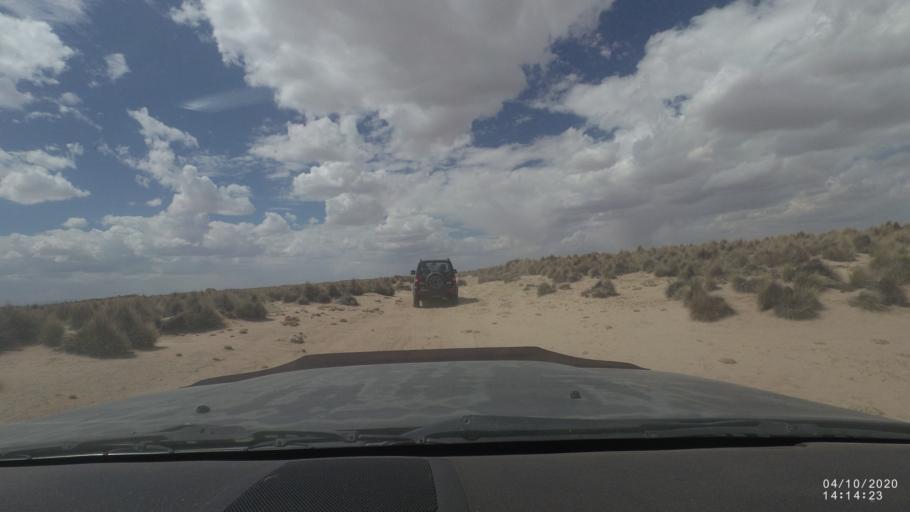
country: BO
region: Oruro
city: Poopo
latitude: -18.6953
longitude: -67.4548
